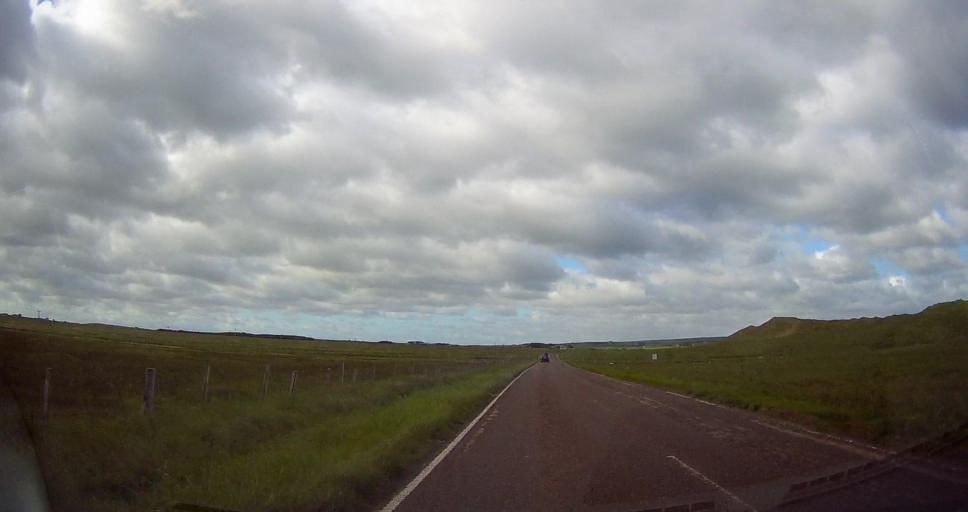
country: GB
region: Scotland
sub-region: Highland
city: Thurso
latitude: 58.6022
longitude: -3.3494
